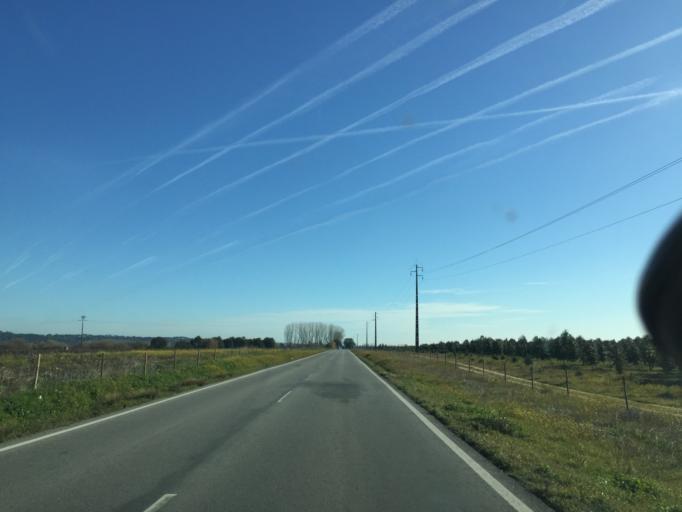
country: PT
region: Santarem
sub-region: Coruche
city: Coruche
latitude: 38.9793
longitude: -8.4430
